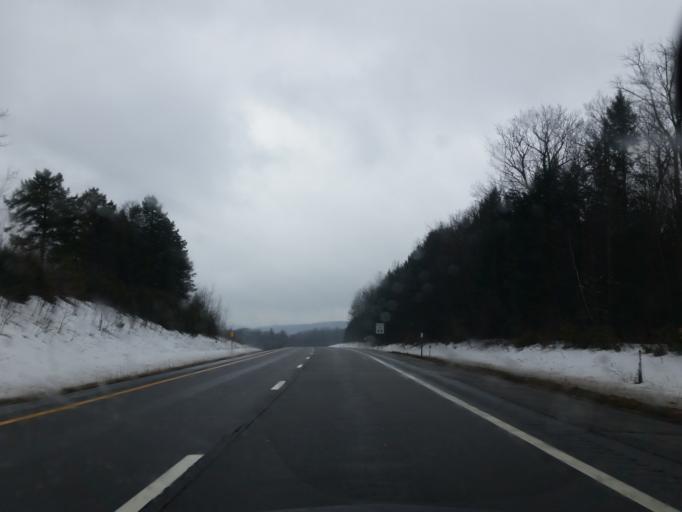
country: US
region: New York
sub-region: Chenango County
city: Lakeview
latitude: 42.3652
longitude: -75.9954
